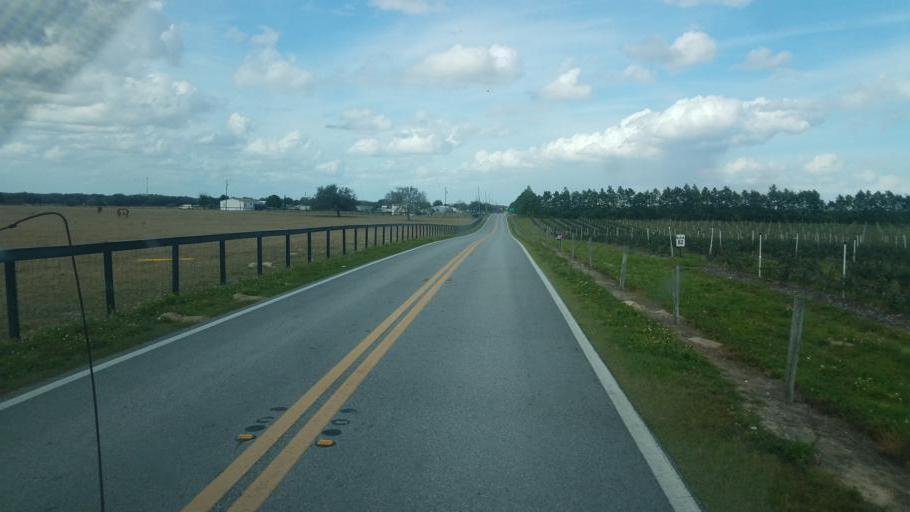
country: US
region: Florida
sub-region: Polk County
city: Lake Hamilton
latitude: 28.0677
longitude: -81.5789
